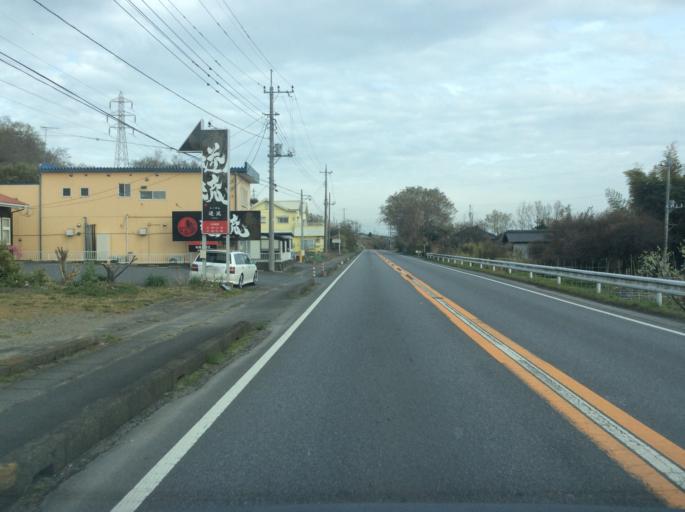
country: JP
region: Ibaraki
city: Tsukuba
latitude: 36.1553
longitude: 140.1130
